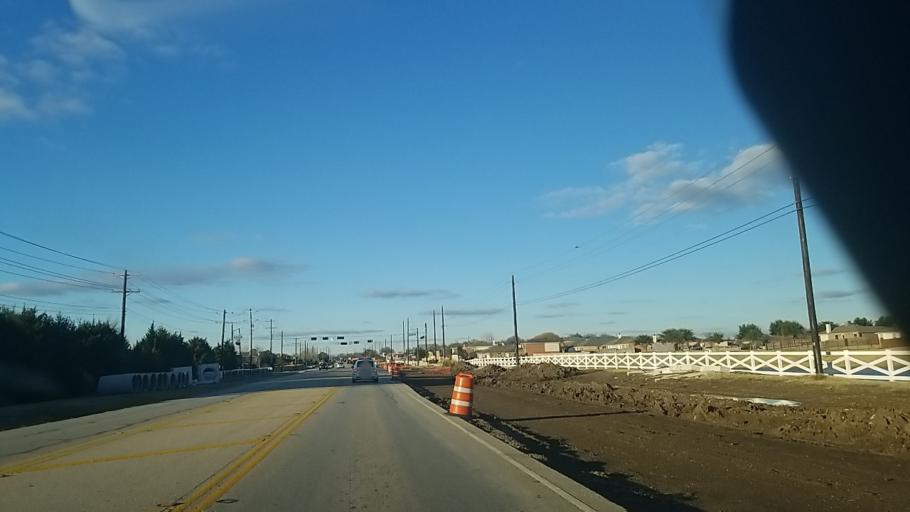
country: US
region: Texas
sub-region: Denton County
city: Corinth
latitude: 33.1526
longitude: -97.1054
